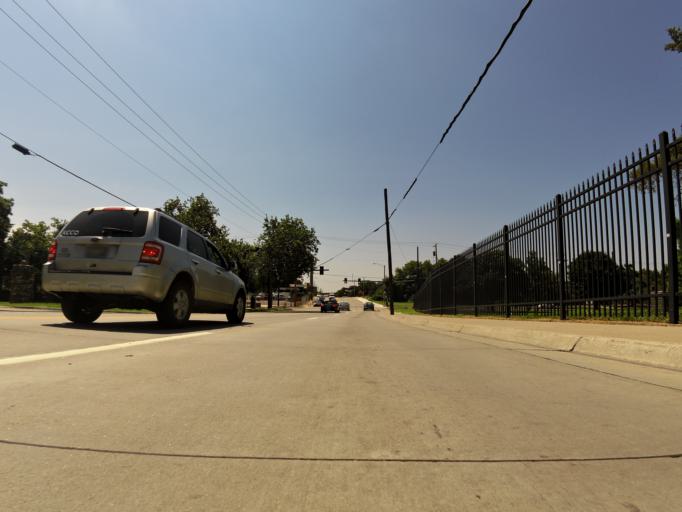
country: US
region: Kansas
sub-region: Sedgwick County
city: Wichita
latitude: 37.7017
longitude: -97.2991
